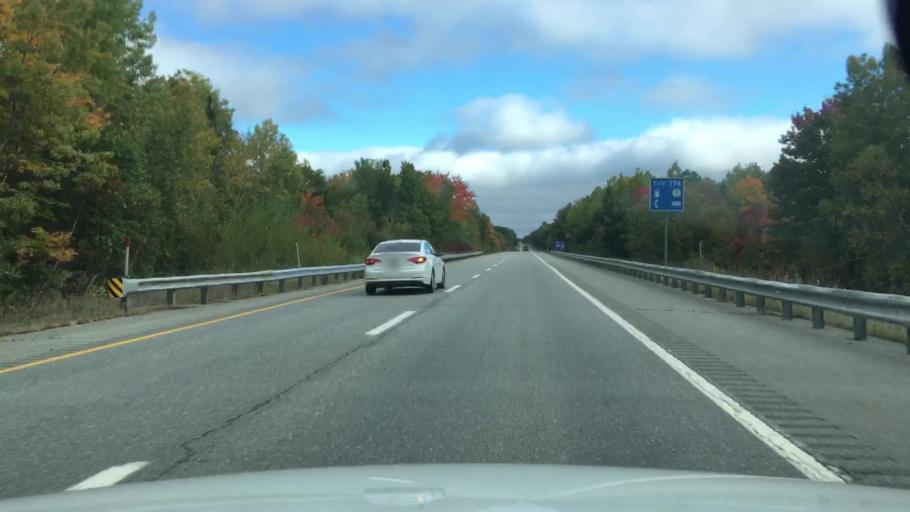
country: US
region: Maine
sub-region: Penobscot County
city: Carmel
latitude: 44.7668
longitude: -68.9953
